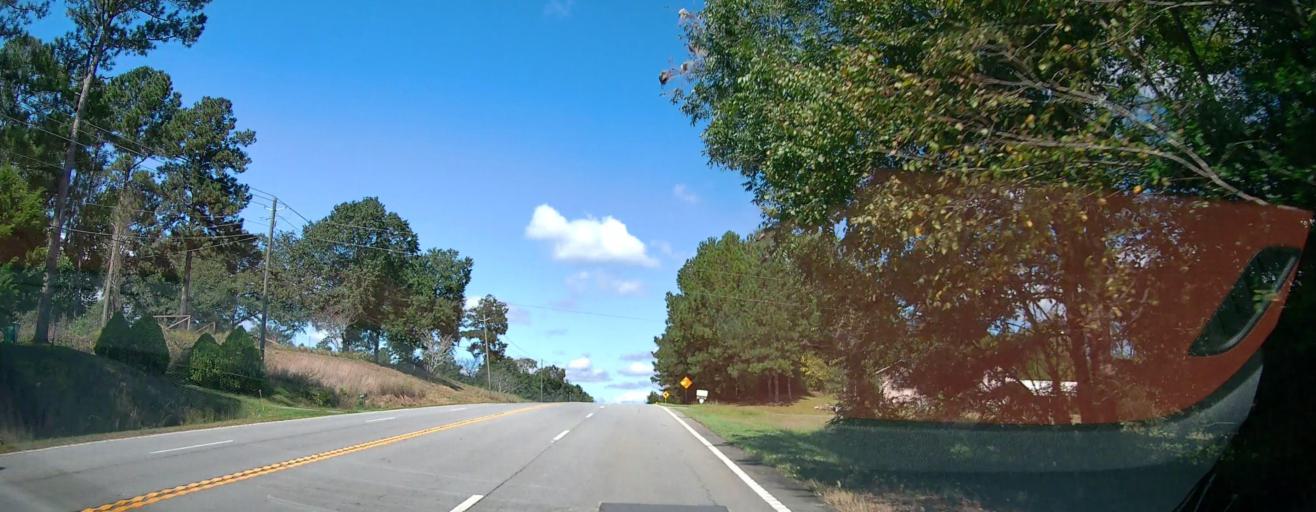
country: US
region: Georgia
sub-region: Bibb County
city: Macon
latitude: 32.7754
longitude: -83.5634
